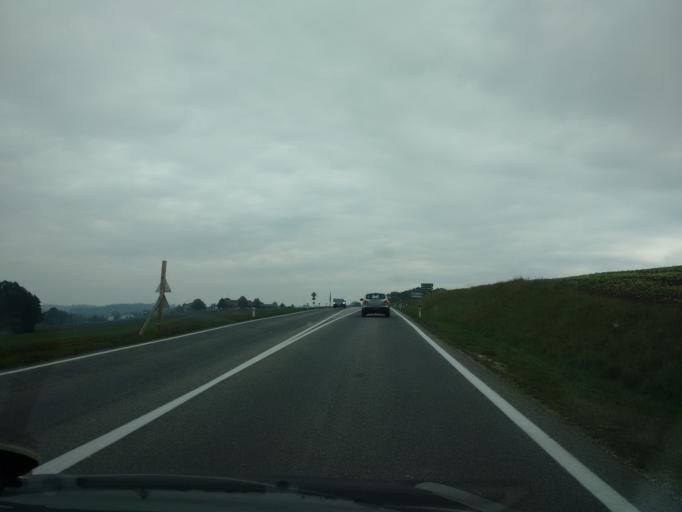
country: AT
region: Upper Austria
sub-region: Politischer Bezirk Steyr-Land
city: Pfarrkirchen bei Bad Hall
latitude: 48.0591
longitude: 14.1750
